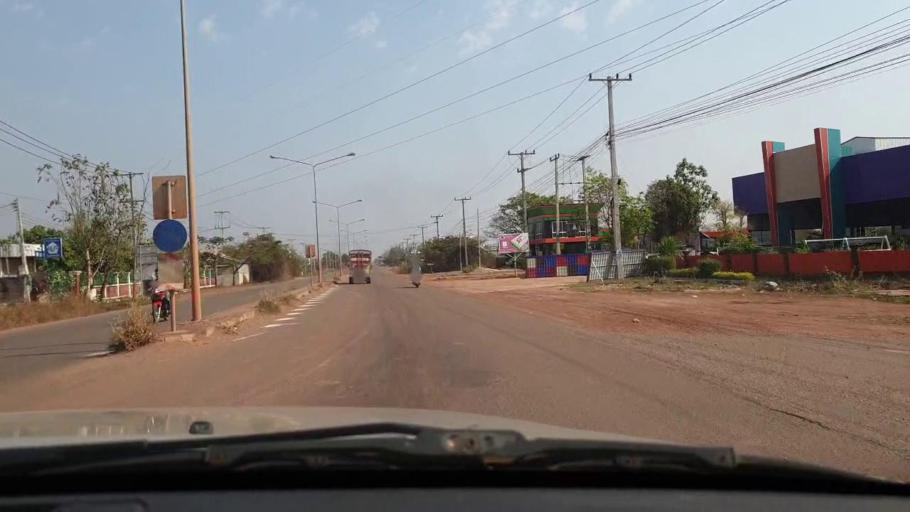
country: LA
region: Vientiane
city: Vientiane
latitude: 18.0100
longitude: 102.7217
